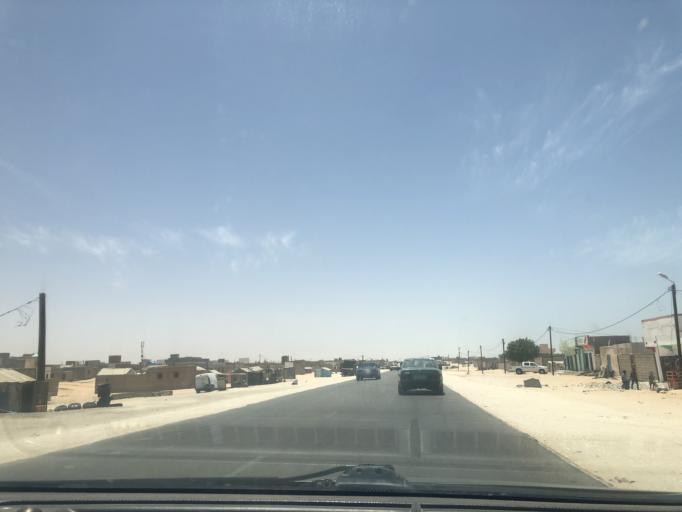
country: MR
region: Nouakchott
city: Nouakchott
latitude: 18.0126
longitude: -15.9592
